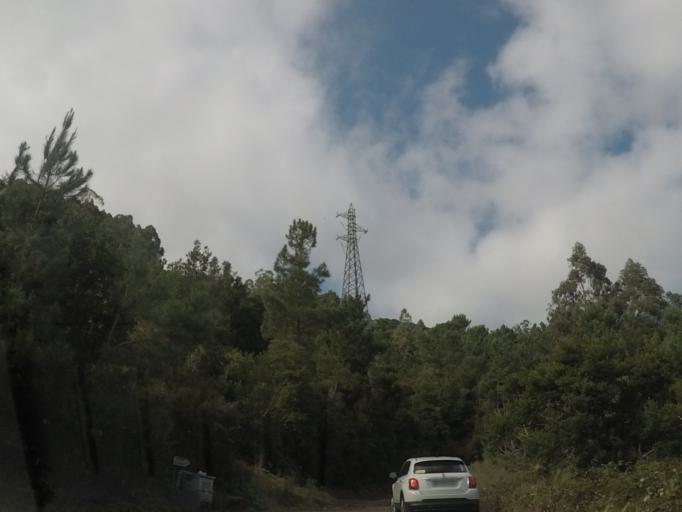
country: PT
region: Madeira
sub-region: Sao Vicente
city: Sao Vicente
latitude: 32.7799
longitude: -17.0481
